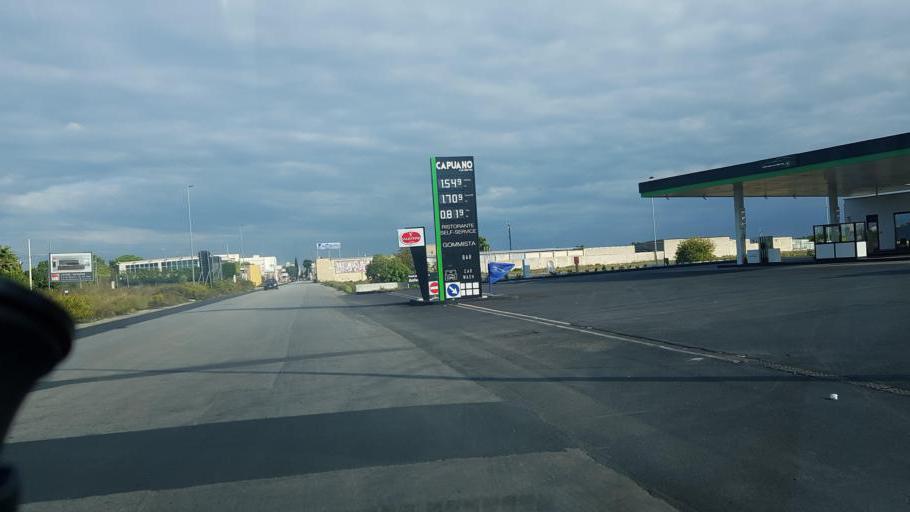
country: IT
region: Apulia
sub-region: Provincia di Brindisi
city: Francavilla Fontana
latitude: 40.5304
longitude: 17.5690
